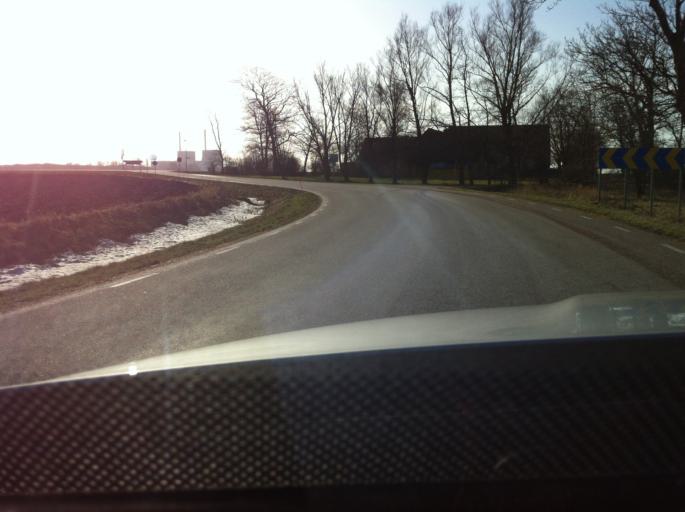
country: SE
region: Skane
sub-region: Kavlinge Kommun
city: Hofterup
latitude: 55.7602
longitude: 12.9185
